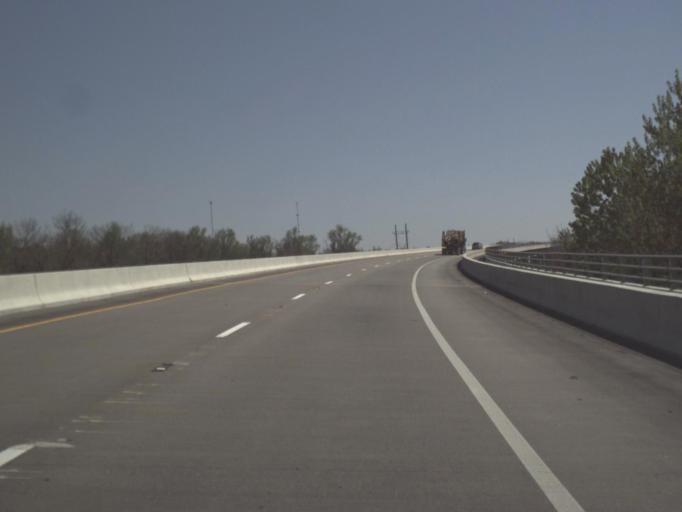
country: US
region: Florida
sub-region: Liberty County
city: Bristol
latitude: 30.4406
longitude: -85.0035
